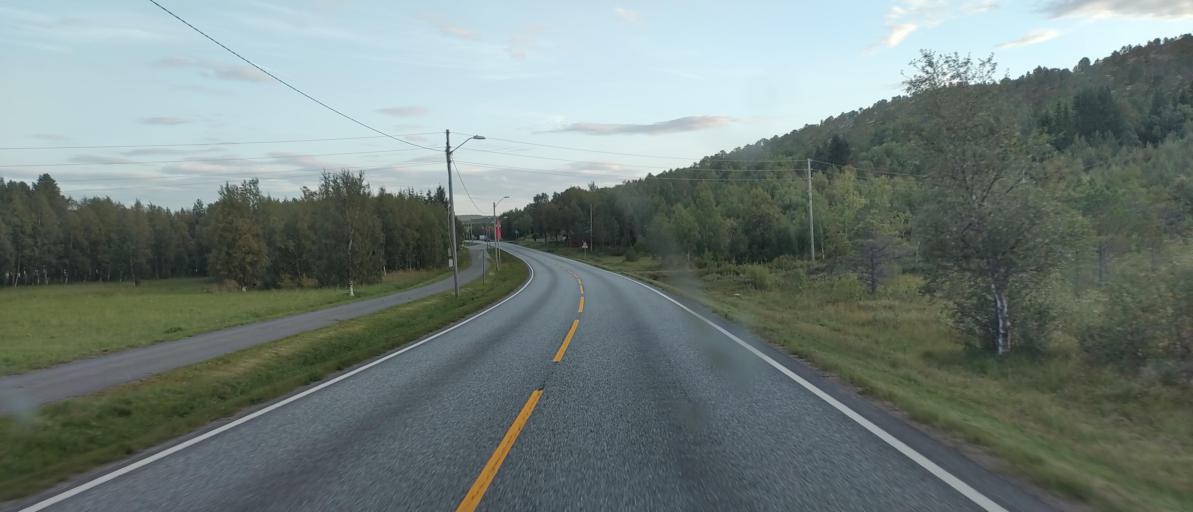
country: NO
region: Nordland
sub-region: Lodingen
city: Lodingen
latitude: 68.1995
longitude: 16.0597
